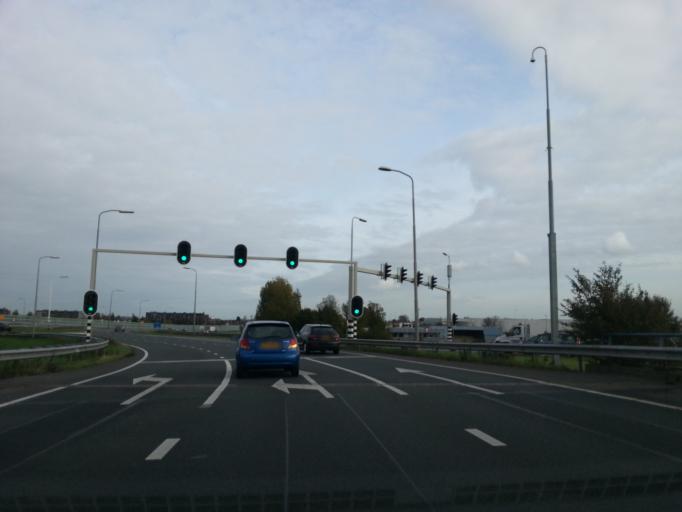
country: NL
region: South Holland
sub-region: Gemeente Delft
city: Delft
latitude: 51.9957
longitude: 4.3898
